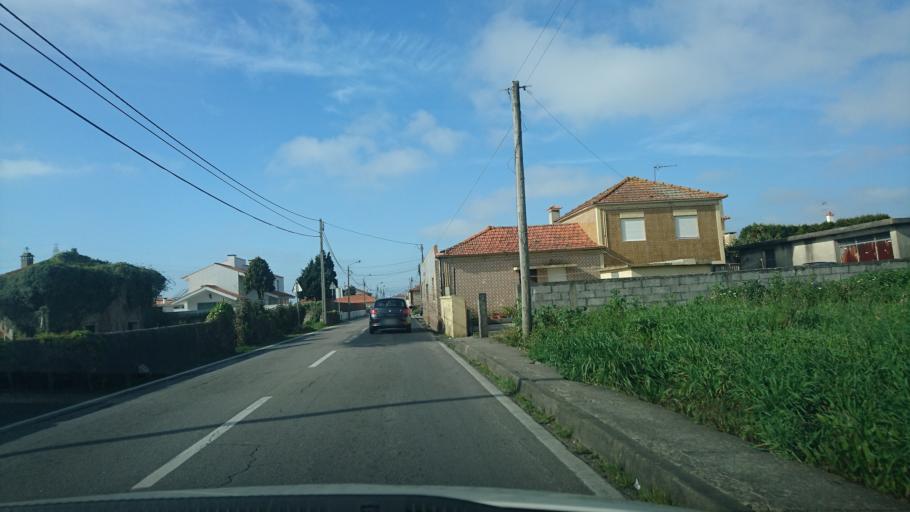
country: PT
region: Aveiro
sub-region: Espinho
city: Silvalde
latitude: 40.9937
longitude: -8.6315
